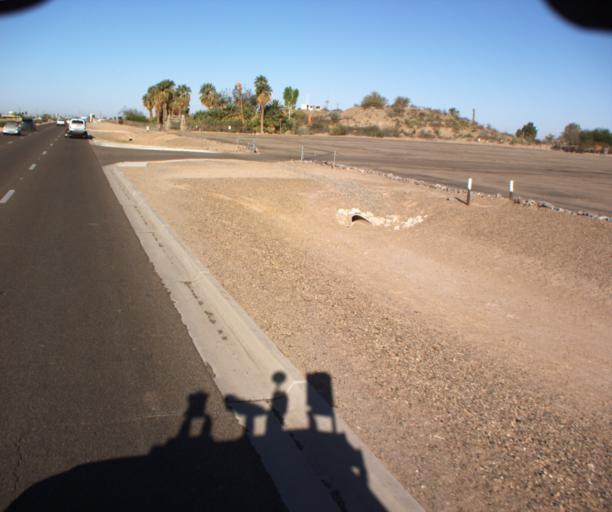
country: US
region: Arizona
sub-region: Yuma County
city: Yuma
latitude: 32.6696
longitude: -114.5922
